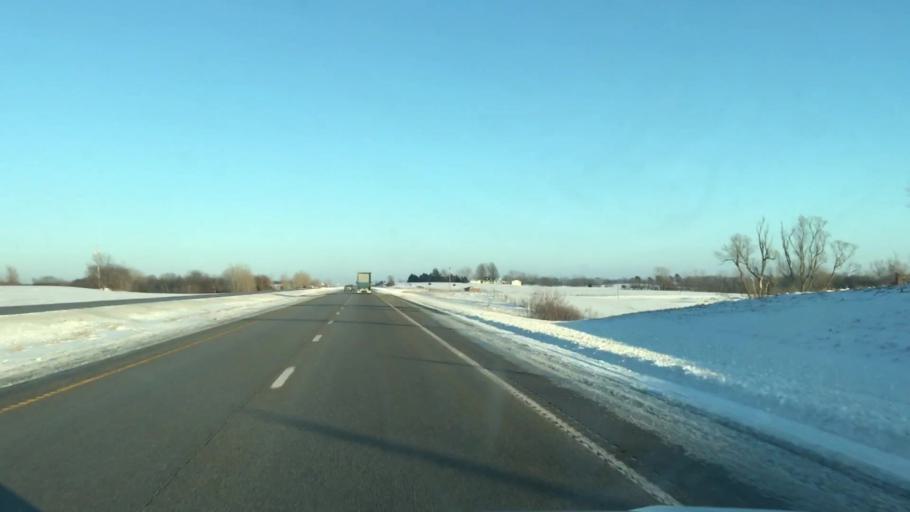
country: US
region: Missouri
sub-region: Clinton County
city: Gower
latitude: 39.7470
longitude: -94.6229
